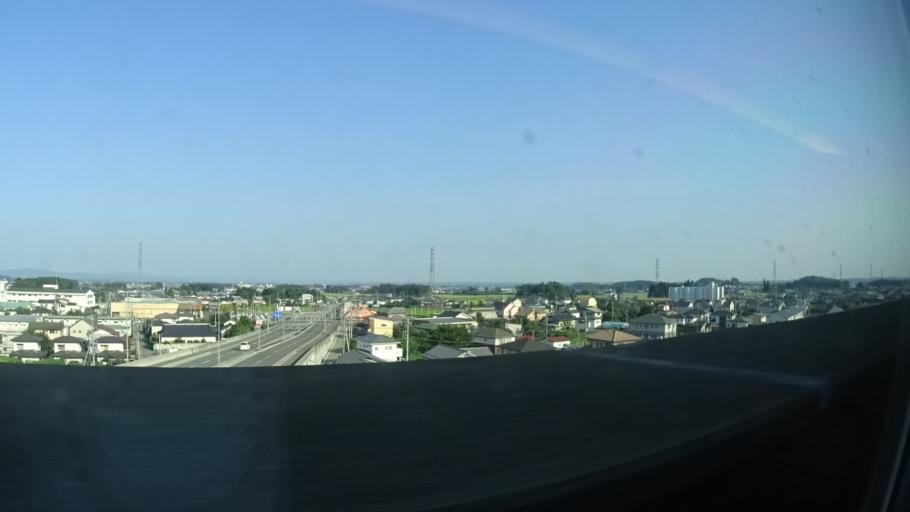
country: JP
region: Tochigi
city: Otawara
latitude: 36.8793
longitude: 139.9828
